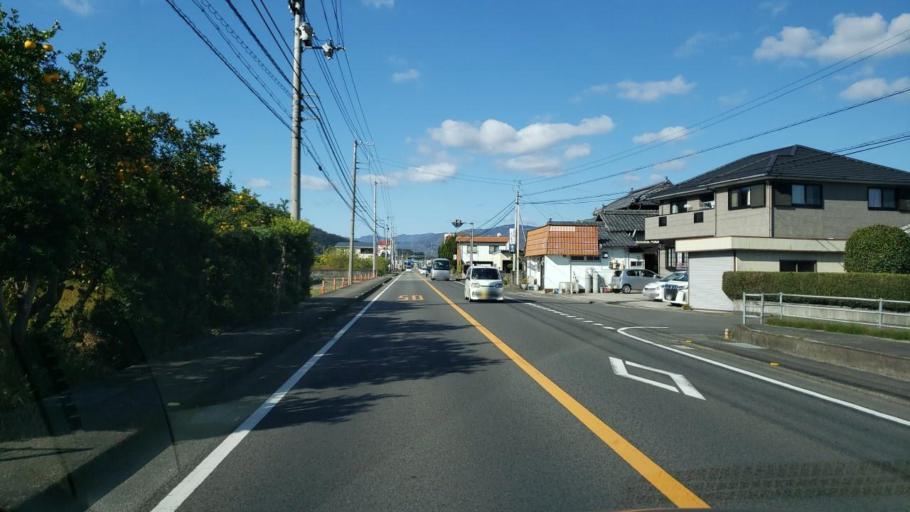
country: JP
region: Tokushima
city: Wakimachi
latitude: 34.0602
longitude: 134.2140
